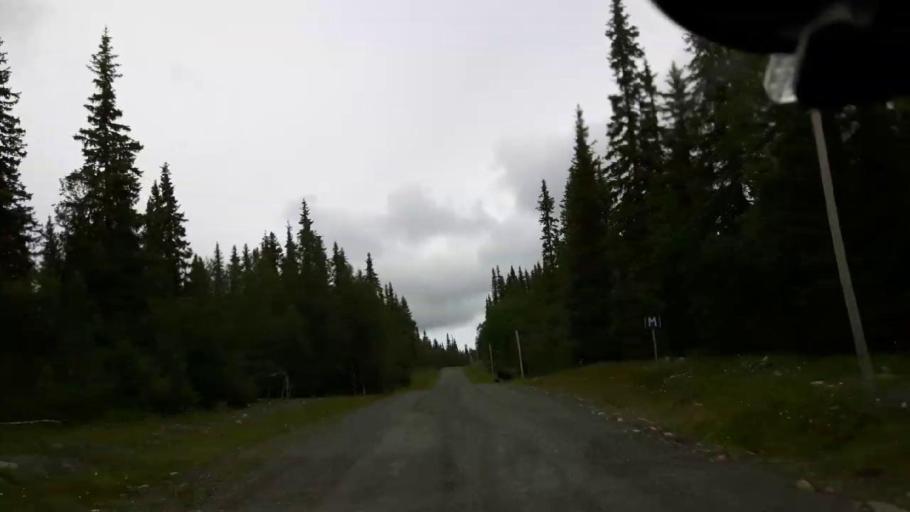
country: SE
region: Jaemtland
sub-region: Krokoms Kommun
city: Valla
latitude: 63.7500
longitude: 13.8355
